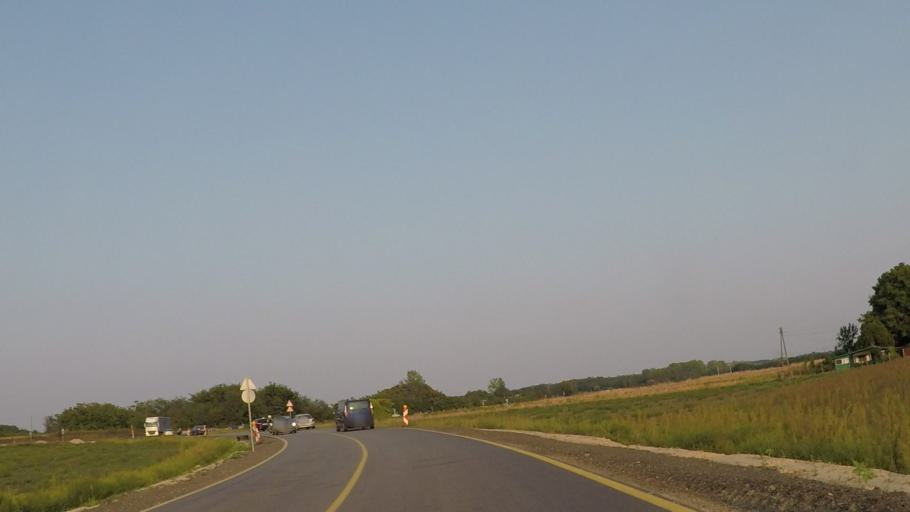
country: HU
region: Pest
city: Albertirsa
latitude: 47.2505
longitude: 19.6391
